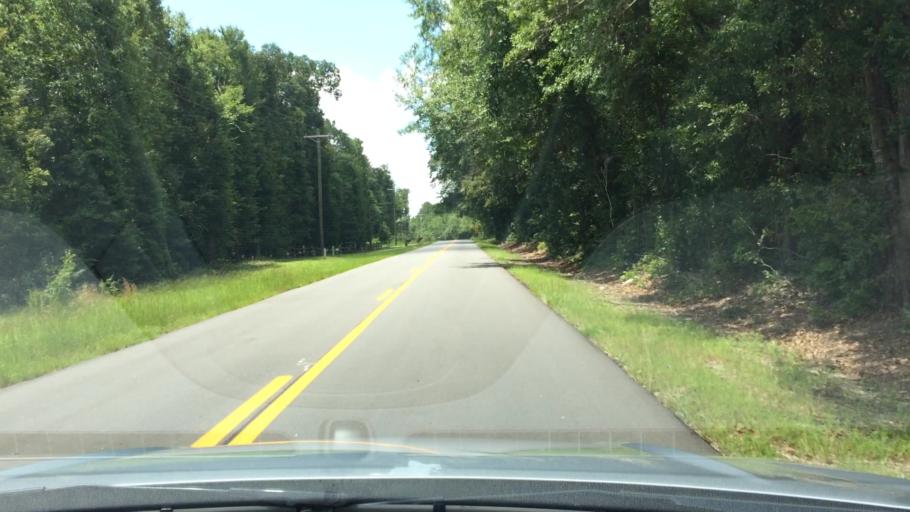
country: US
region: South Carolina
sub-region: Calhoun County
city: Oak Grove
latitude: 33.8043
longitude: -81.0104
